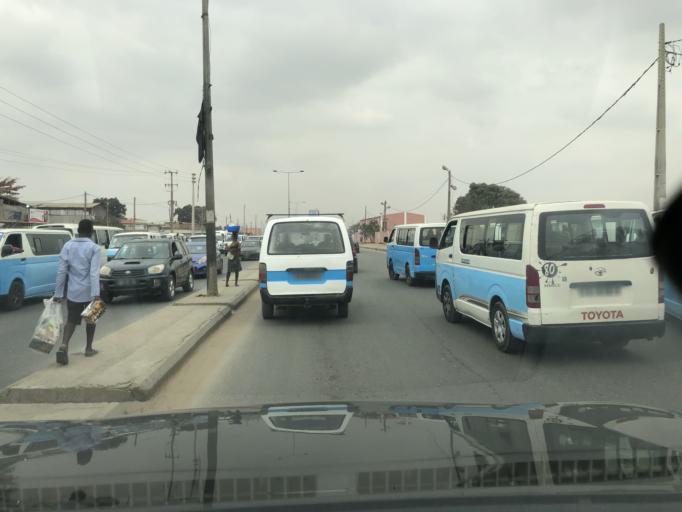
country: AO
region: Luanda
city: Luanda
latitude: -8.8224
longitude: 13.2822
